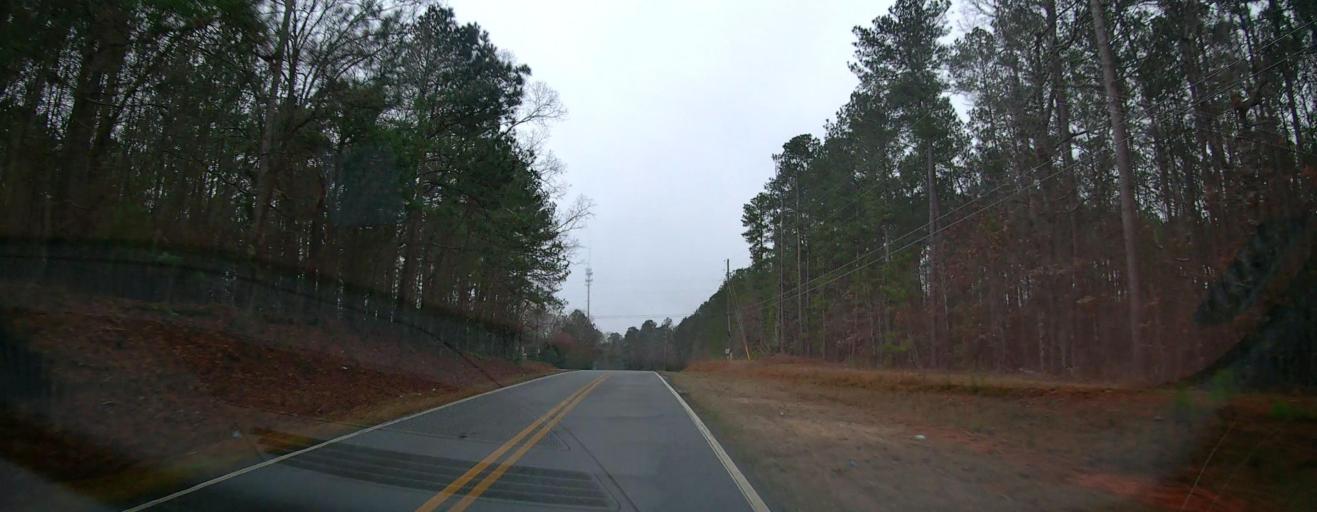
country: US
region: Georgia
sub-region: Monroe County
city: Forsyth
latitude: 33.1154
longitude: -83.9924
